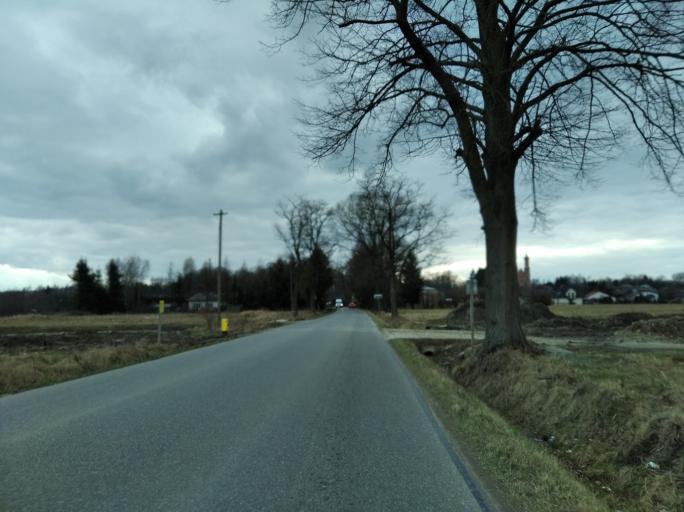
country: PL
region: Subcarpathian Voivodeship
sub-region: Powiat krosnienski
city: Odrzykon
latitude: 49.7496
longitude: 21.7057
